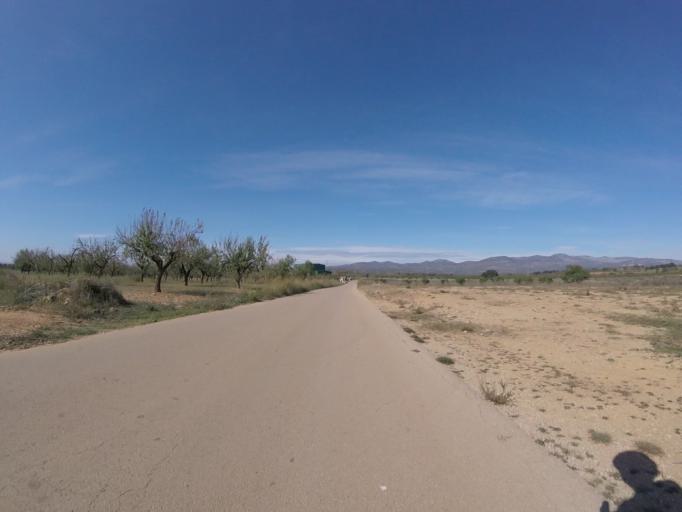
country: ES
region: Valencia
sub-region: Provincia de Castello
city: Benlloch
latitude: 40.2054
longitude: 0.0502
